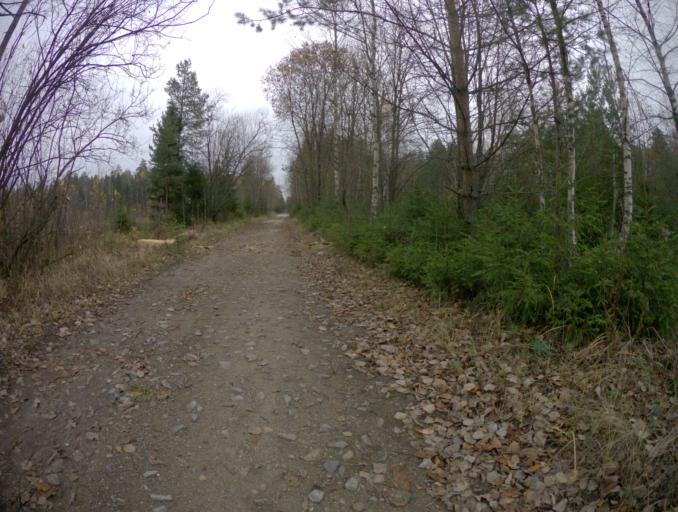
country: RU
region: Vladimir
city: Krasnyy Oktyabr'
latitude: 56.0152
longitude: 38.8538
